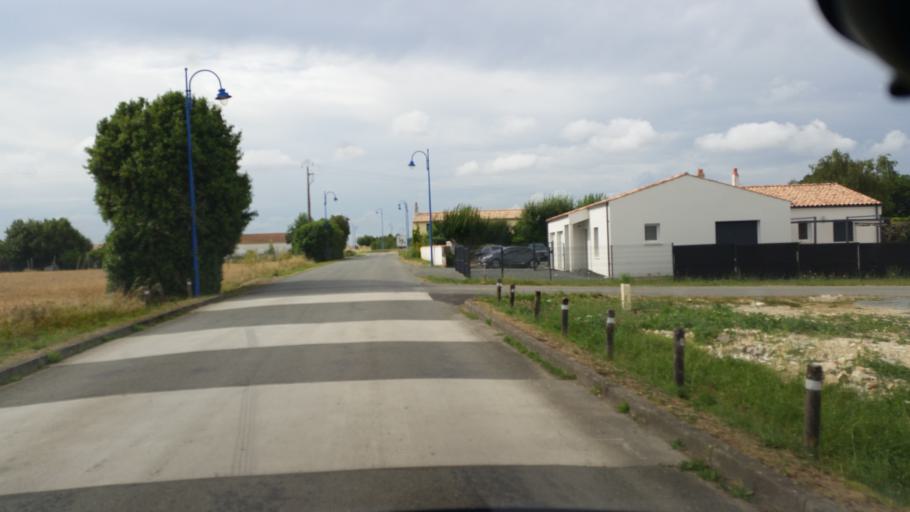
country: FR
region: Poitou-Charentes
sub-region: Departement de la Charente-Maritime
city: Courcon
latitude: 46.1929
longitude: -0.8668
